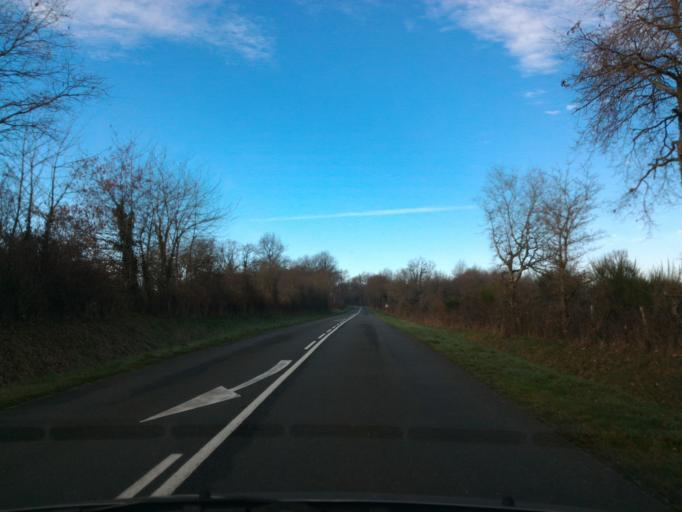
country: FR
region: Poitou-Charentes
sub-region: Departement de la Charente
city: Confolens
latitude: 46.0336
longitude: 0.6199
